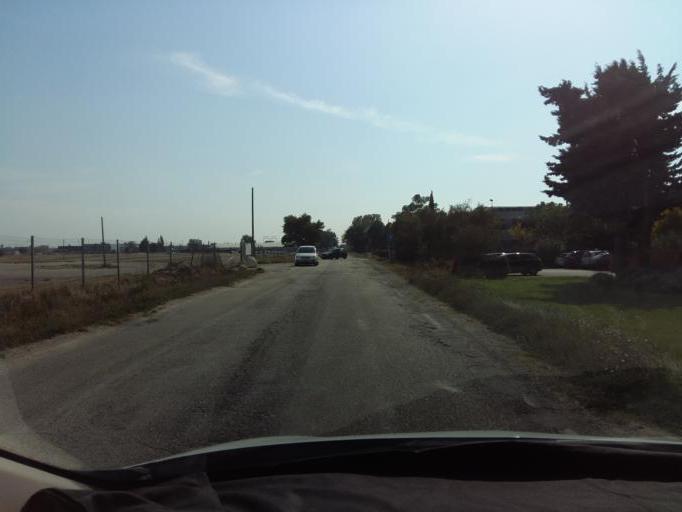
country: FR
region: Provence-Alpes-Cote d'Azur
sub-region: Departement du Vaucluse
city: Montfavet
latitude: 43.9126
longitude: 4.8931
